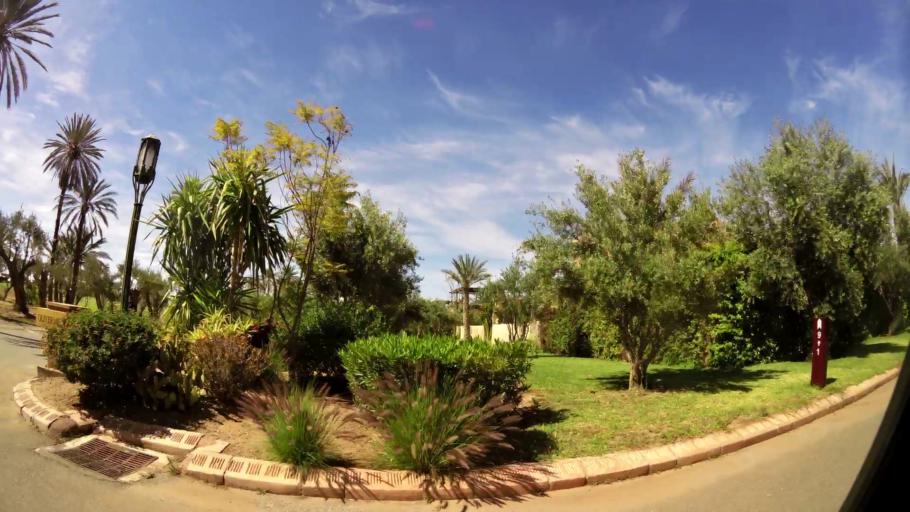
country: MA
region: Marrakech-Tensift-Al Haouz
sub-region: Marrakech
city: Marrakesh
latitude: 31.6176
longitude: -7.9364
